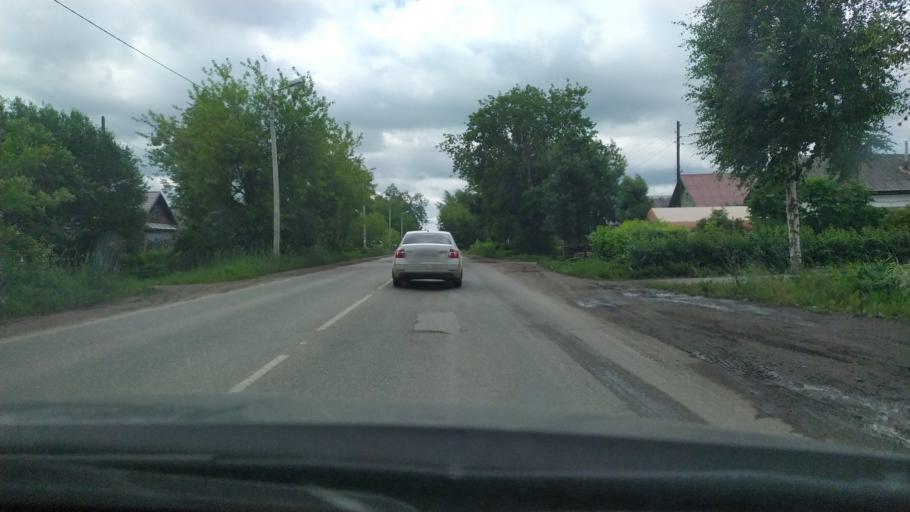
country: RU
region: Perm
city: Perm
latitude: 57.9842
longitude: 56.3044
